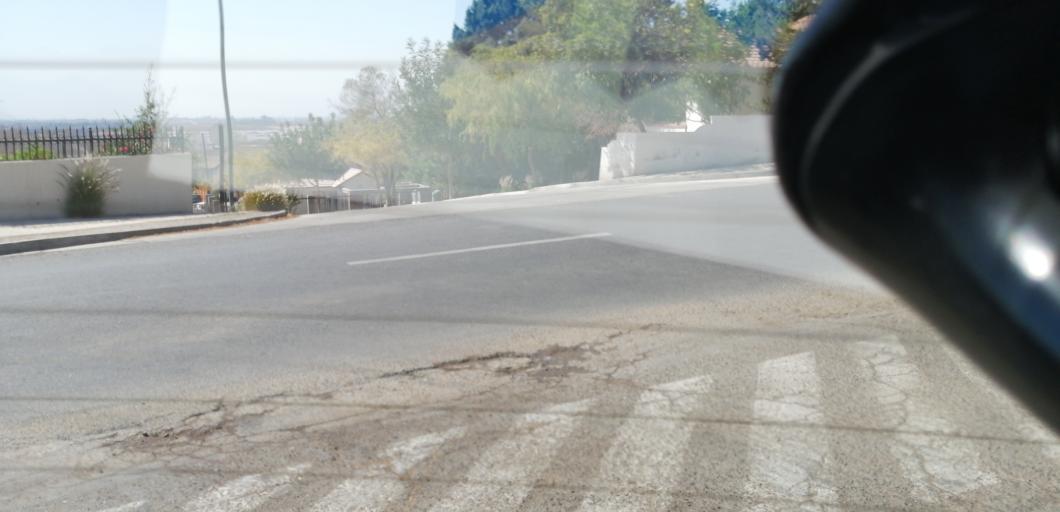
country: CL
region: Santiago Metropolitan
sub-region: Provincia de Santiago
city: Lo Prado
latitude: -33.4542
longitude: -70.8223
